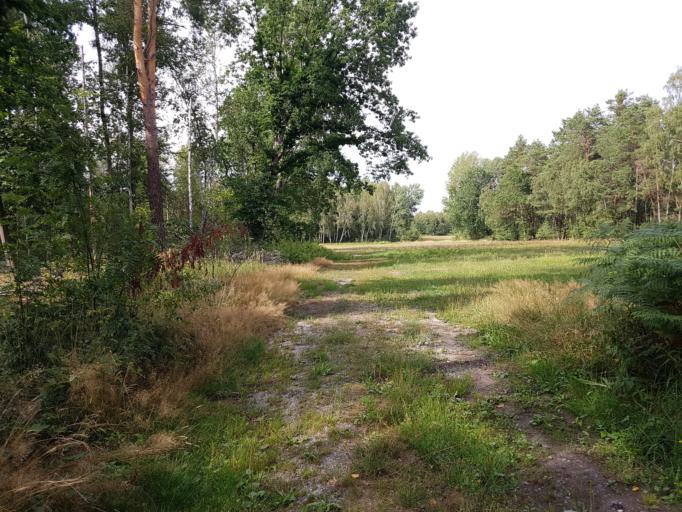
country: DE
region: Brandenburg
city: Doberlug-Kirchhain
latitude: 51.6309
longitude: 13.5970
